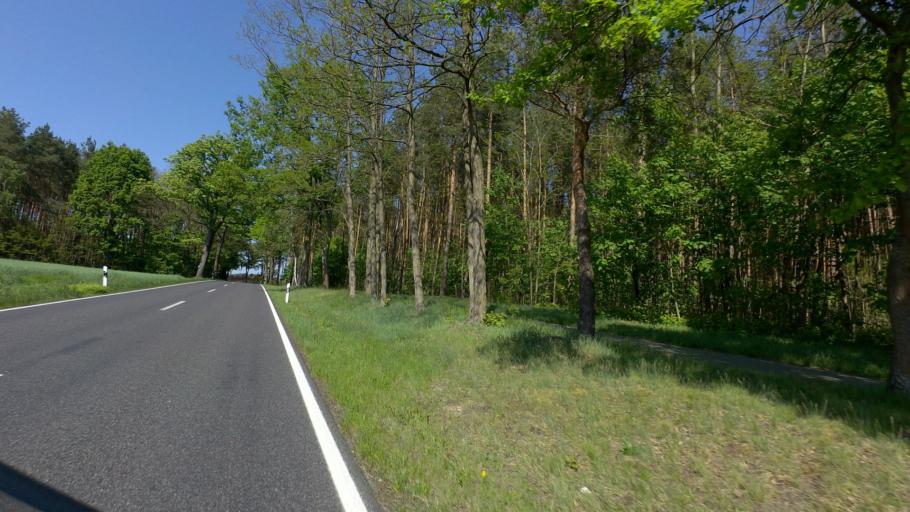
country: DE
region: Brandenburg
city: Neu Zauche
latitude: 52.0266
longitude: 14.0400
